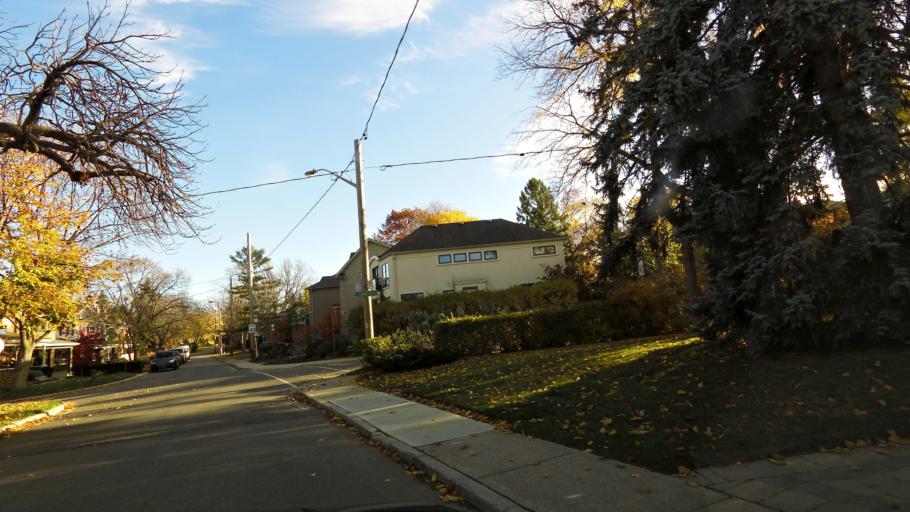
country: CA
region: Ontario
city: Etobicoke
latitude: 43.6610
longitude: -79.5062
